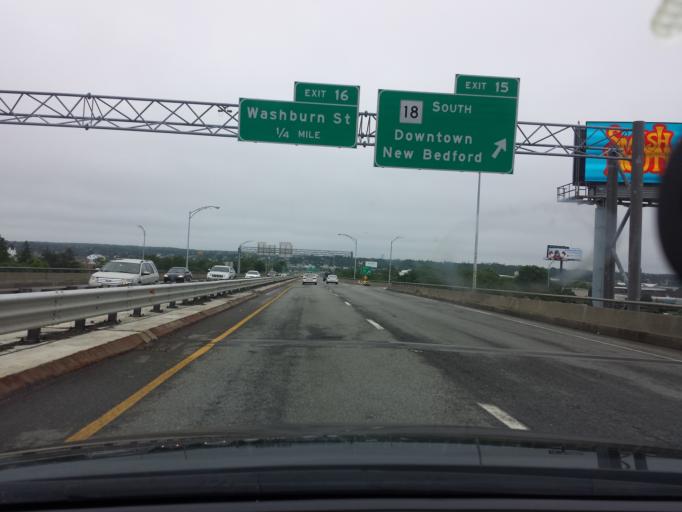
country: US
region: Massachusetts
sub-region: Bristol County
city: New Bedford
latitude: 41.6538
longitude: -70.9311
